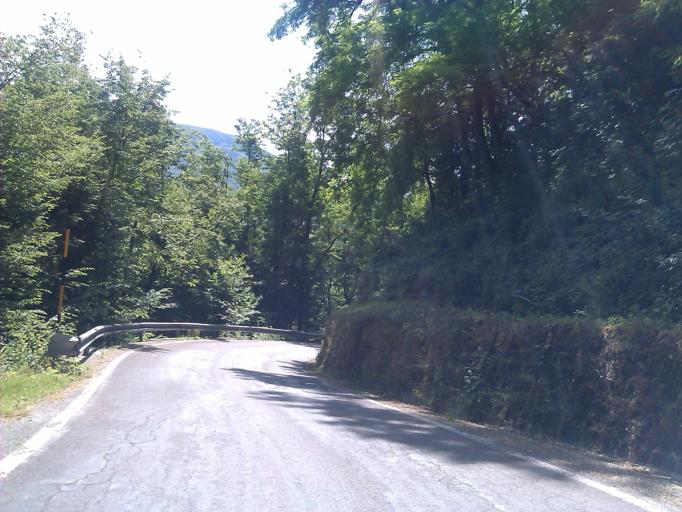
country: IT
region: Tuscany
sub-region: Provincia di Pistoia
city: Sambuca Pistoiese
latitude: 44.1113
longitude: 11.0388
